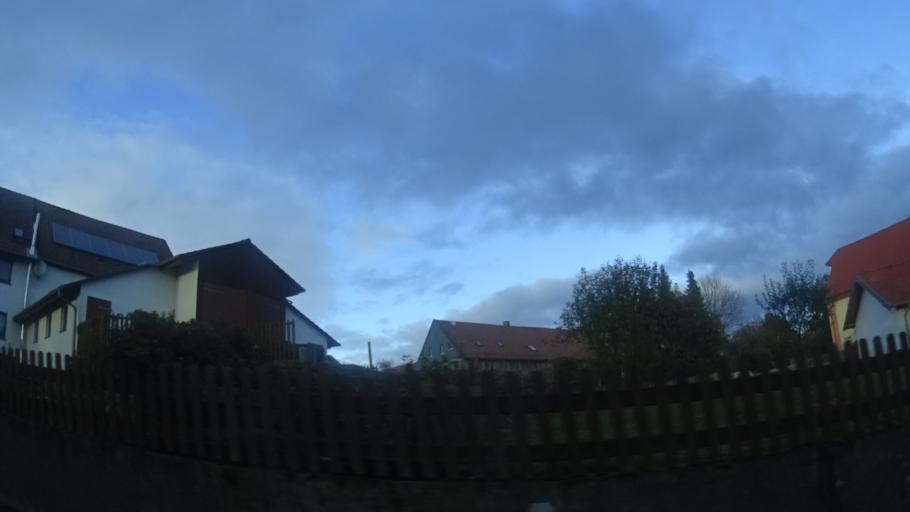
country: DE
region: Hesse
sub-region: Regierungsbezirk Giessen
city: Freiensteinau
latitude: 50.4601
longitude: 9.4280
